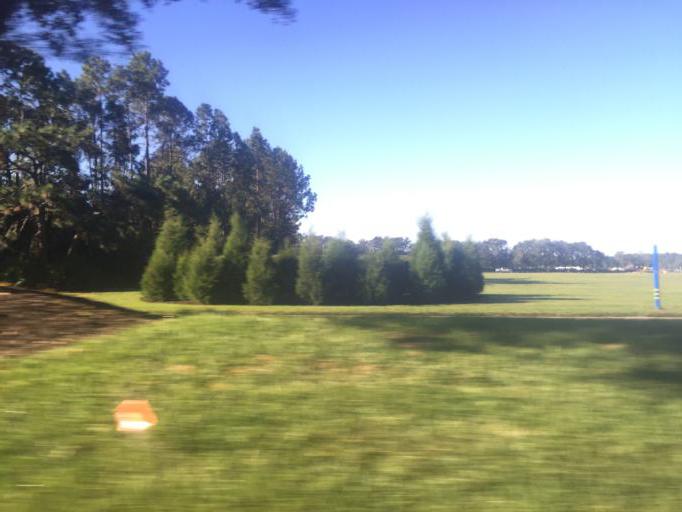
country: US
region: Florida
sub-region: Osceola County
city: Celebration
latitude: 28.3971
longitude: -81.5727
